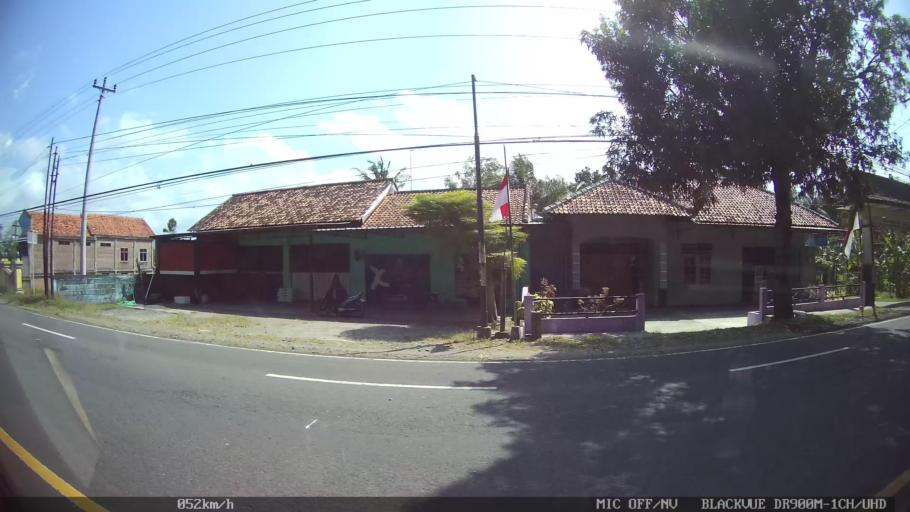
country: ID
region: Daerah Istimewa Yogyakarta
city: Srandakan
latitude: -7.8905
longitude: 110.1152
